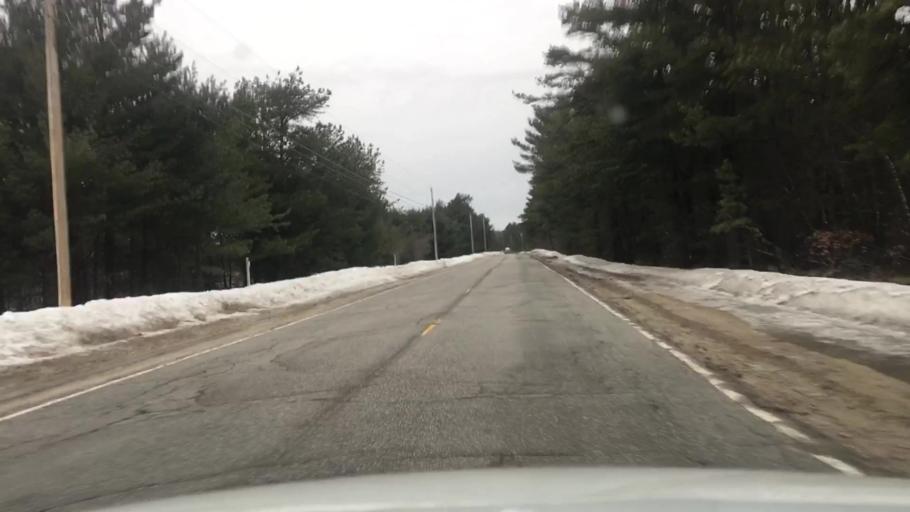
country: US
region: Maine
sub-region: York County
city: Shapleigh
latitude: 43.5924
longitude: -70.8788
